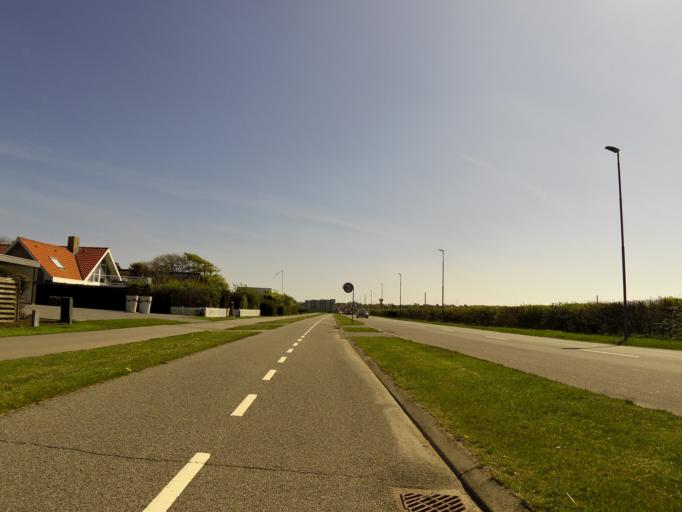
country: DK
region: Central Jutland
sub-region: Struer Kommune
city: Struer
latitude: 56.5014
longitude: 8.5822
